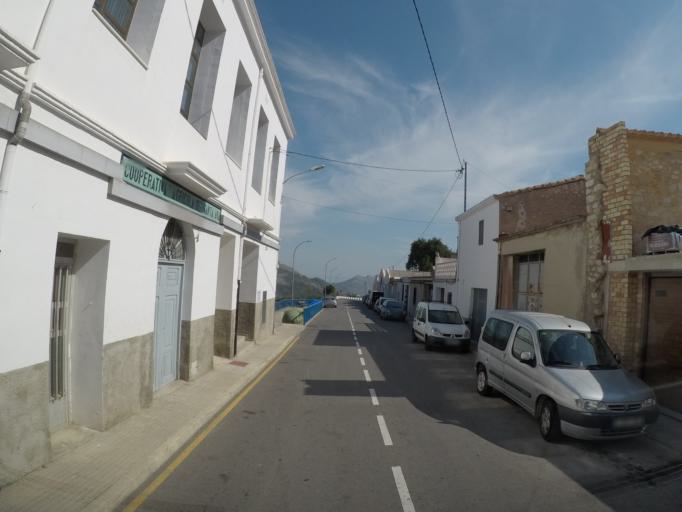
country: ES
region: Valencia
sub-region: Provincia de Alicante
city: Murla
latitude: 38.7803
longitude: -0.1024
